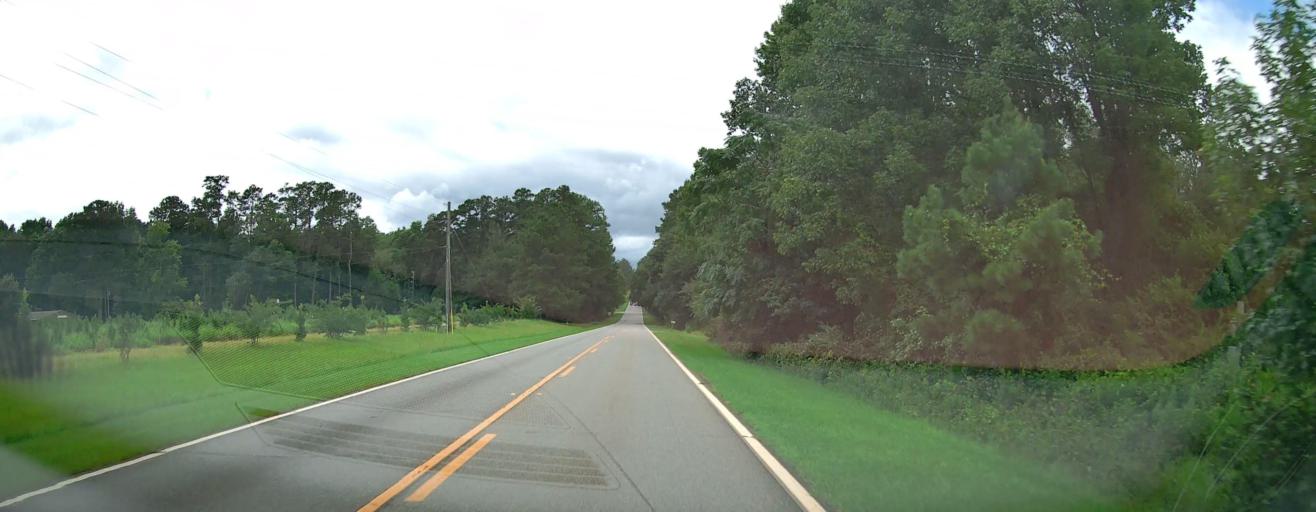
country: US
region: Georgia
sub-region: Twiggs County
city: Jeffersonville
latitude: 32.6798
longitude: -83.3184
